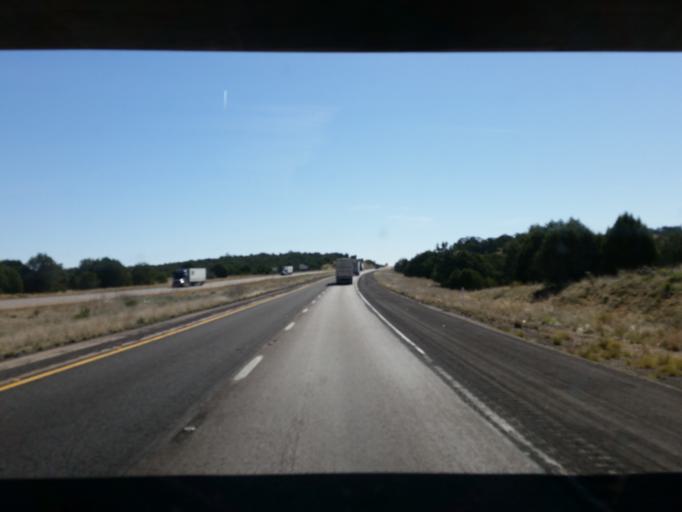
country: US
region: Arizona
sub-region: Mohave County
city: Peach Springs
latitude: 35.2892
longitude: -113.0872
